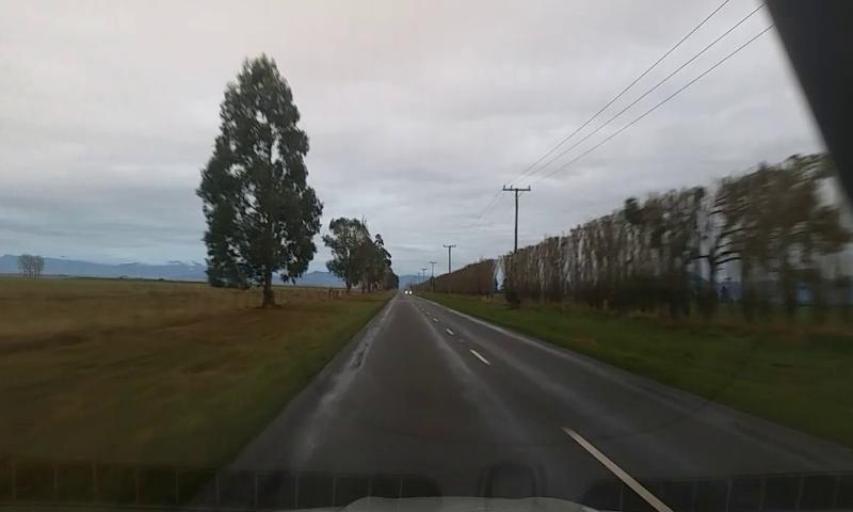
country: NZ
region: Canterbury
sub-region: Ashburton District
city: Methven
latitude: -43.7397
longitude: 171.6844
